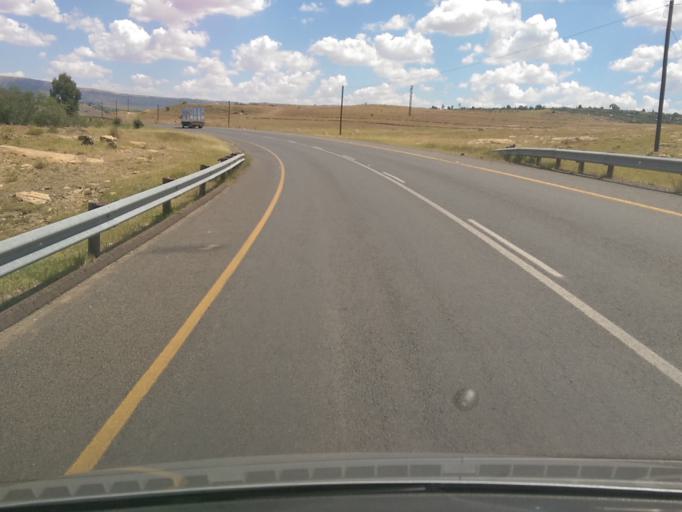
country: LS
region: Maseru
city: Maseru
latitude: -29.3904
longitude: 27.5491
